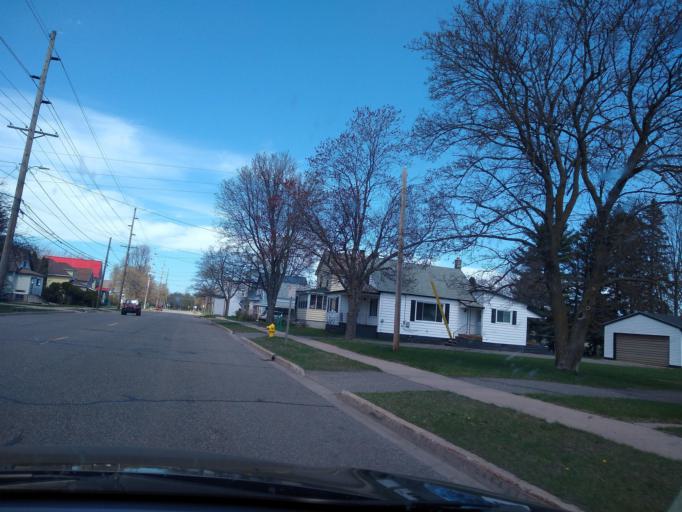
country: US
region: Michigan
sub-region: Marquette County
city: Marquette
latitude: 46.5685
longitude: -87.3961
